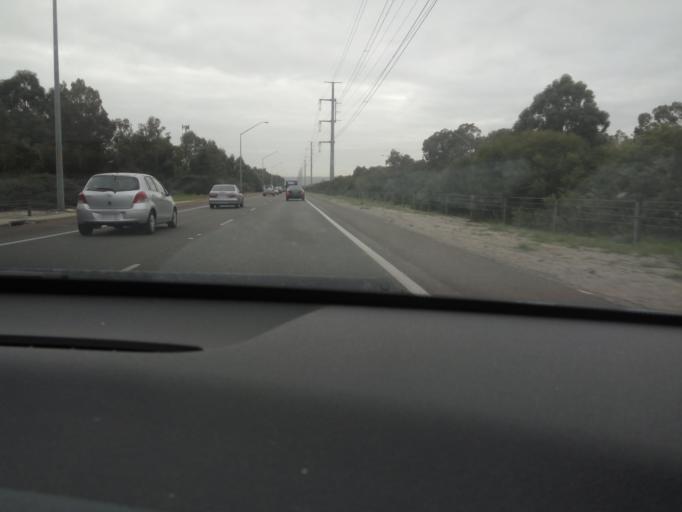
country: AU
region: Western Australia
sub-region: Gosnells
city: Langford
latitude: -32.0491
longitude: 115.9409
